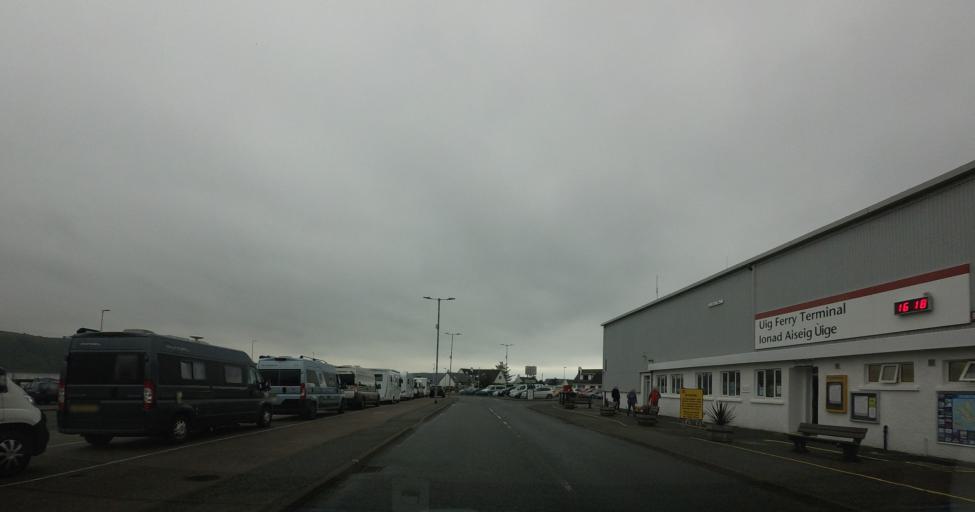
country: GB
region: Scotland
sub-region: Highland
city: Portree
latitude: 57.5871
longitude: -6.3764
